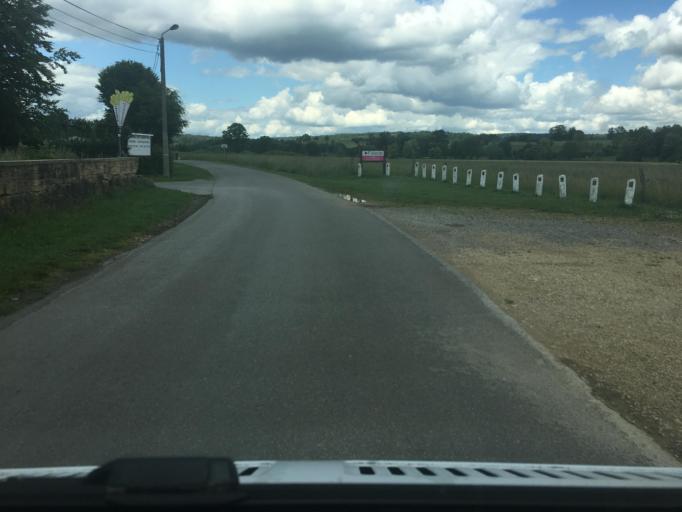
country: BE
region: Wallonia
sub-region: Province du Luxembourg
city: Florenville
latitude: 49.7106
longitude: 5.2618
